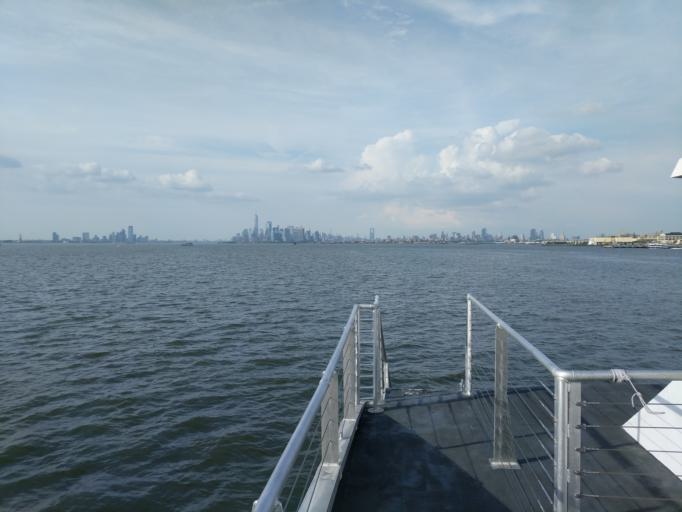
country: US
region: New York
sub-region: Kings County
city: Bensonhurst
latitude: 40.6446
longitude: -74.0361
